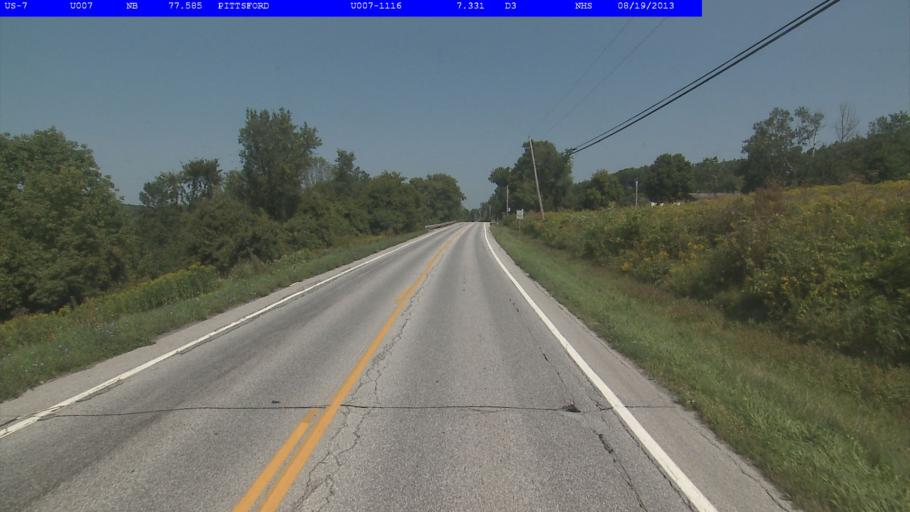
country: US
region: Vermont
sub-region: Rutland County
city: Brandon
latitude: 43.7506
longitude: -73.0477
